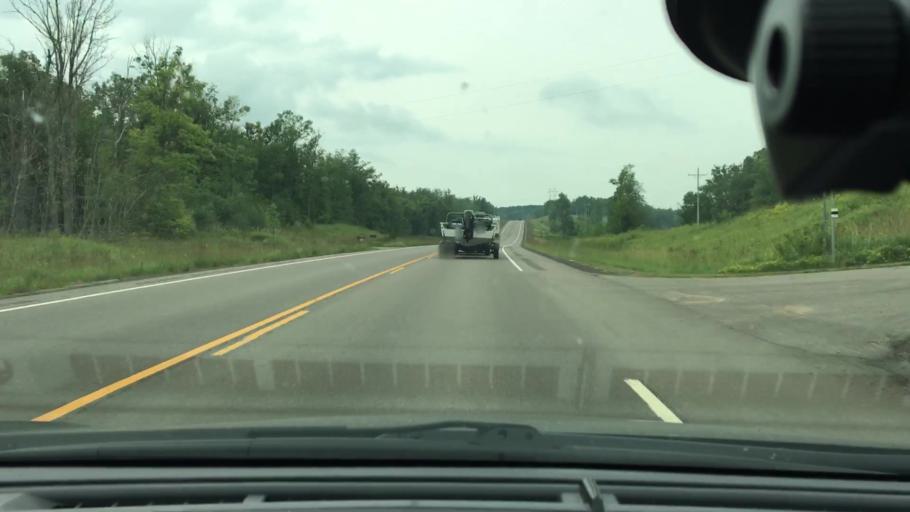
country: US
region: Minnesota
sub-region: Crow Wing County
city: Crosby
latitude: 46.6088
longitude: -93.9496
